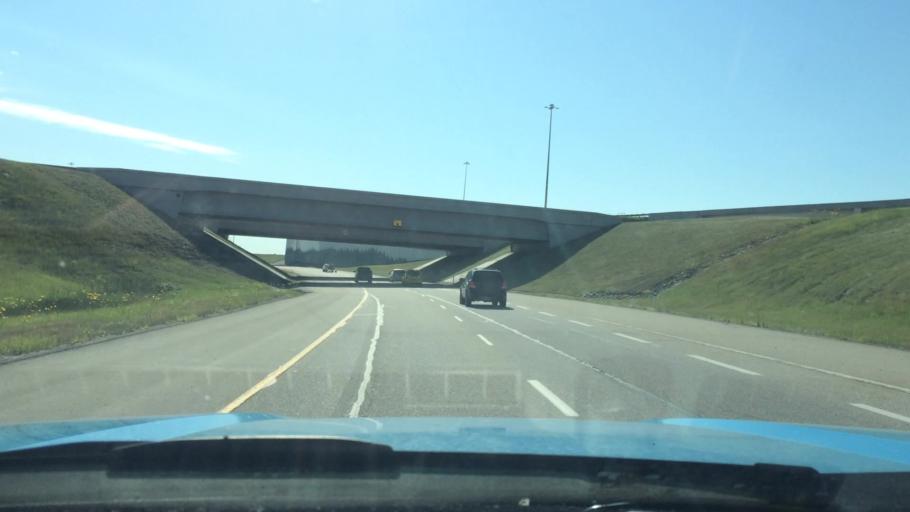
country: CA
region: Alberta
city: Airdrie
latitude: 51.1743
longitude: -114.0028
